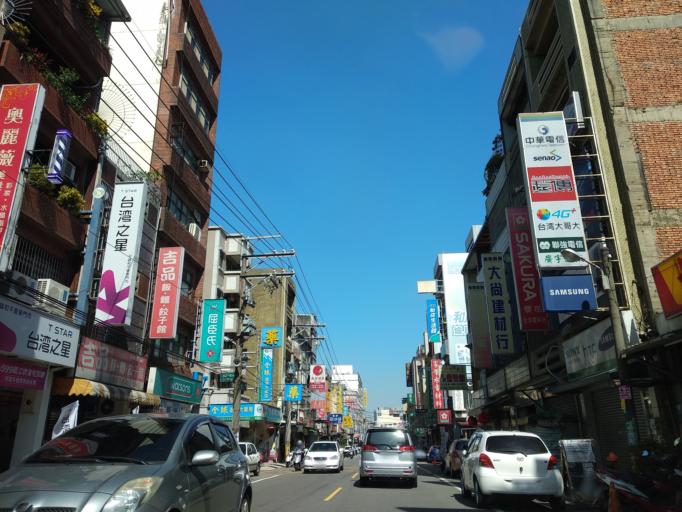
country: TW
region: Taiwan
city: Taoyuan City
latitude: 24.9463
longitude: 121.2198
